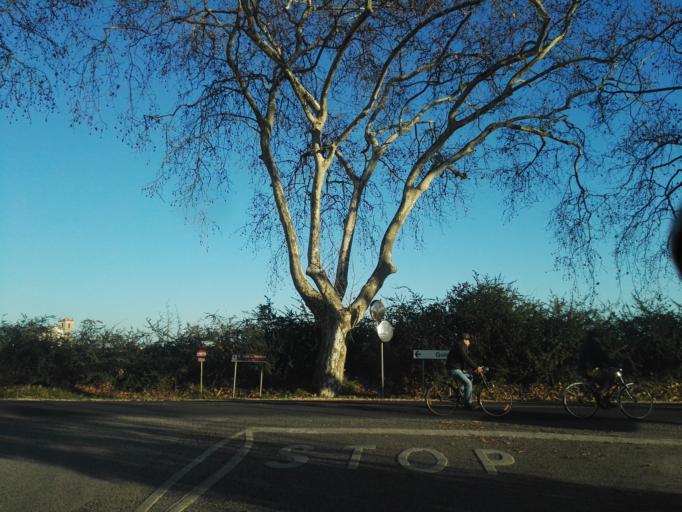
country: PT
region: Santarem
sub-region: Golega
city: Golega
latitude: 39.3568
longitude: -8.5274
